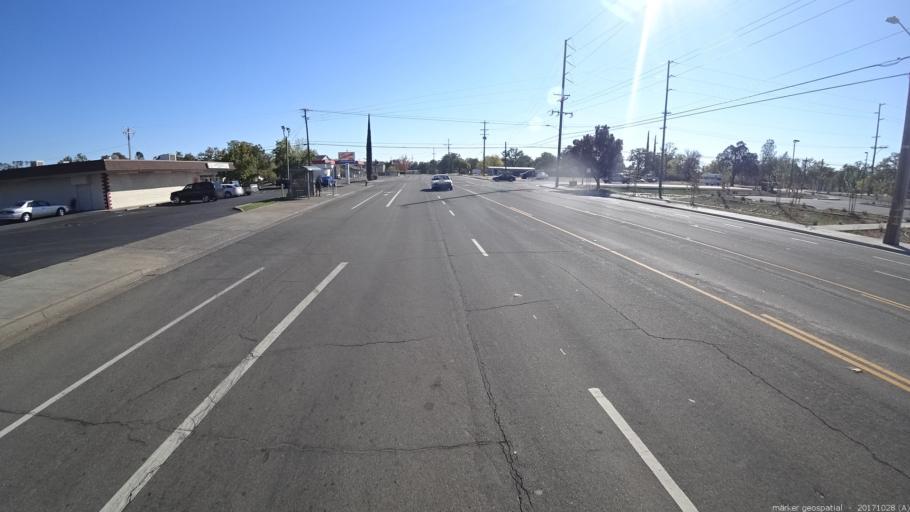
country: US
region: California
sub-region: Shasta County
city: Redding
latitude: 40.6262
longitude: -122.4050
